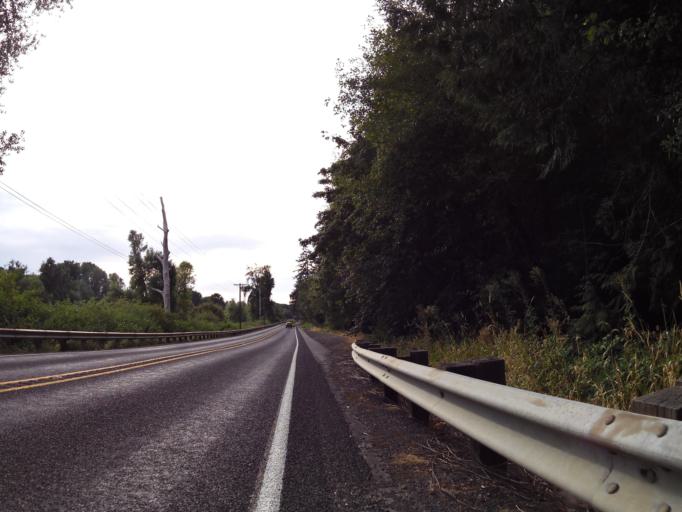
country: US
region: Washington
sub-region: Cowlitz County
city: West Longview
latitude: 46.1885
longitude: -123.0959
